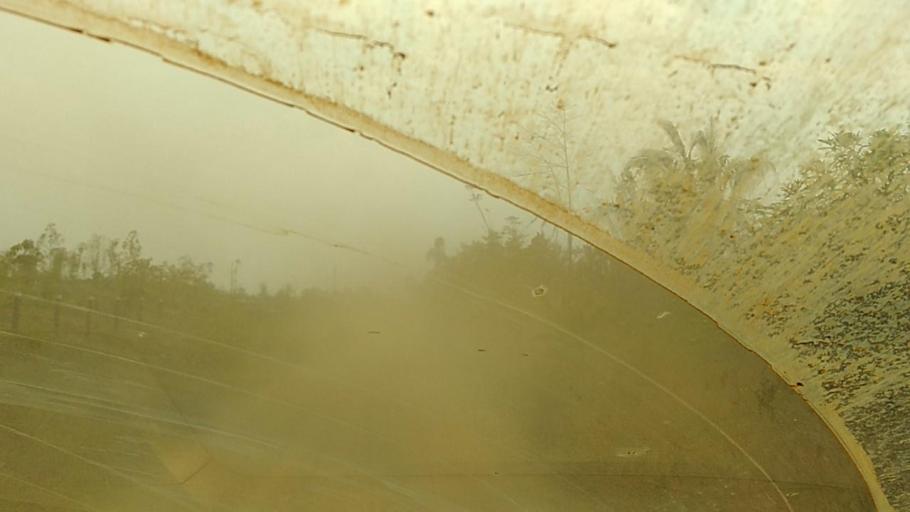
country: BR
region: Rondonia
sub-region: Porto Velho
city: Porto Velho
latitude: -8.7731
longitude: -63.2013
